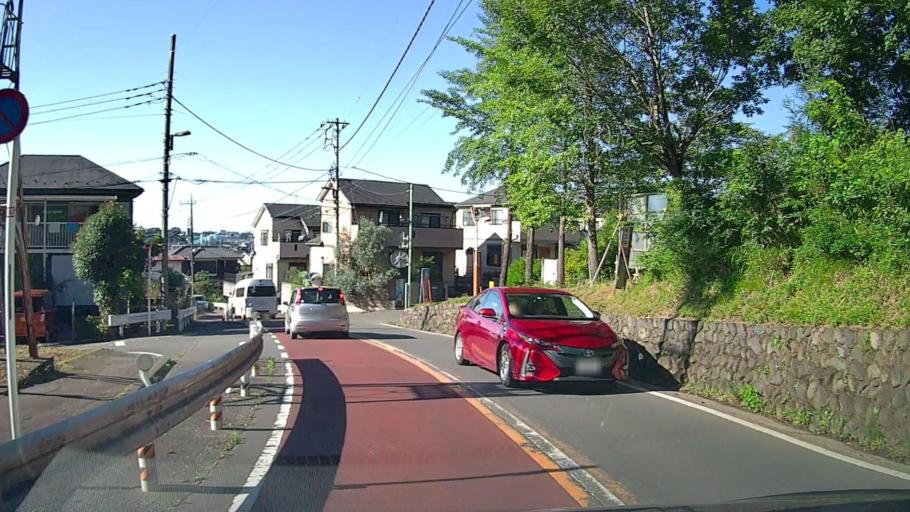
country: JP
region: Tokyo
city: Fussa
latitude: 35.7821
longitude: 139.3639
